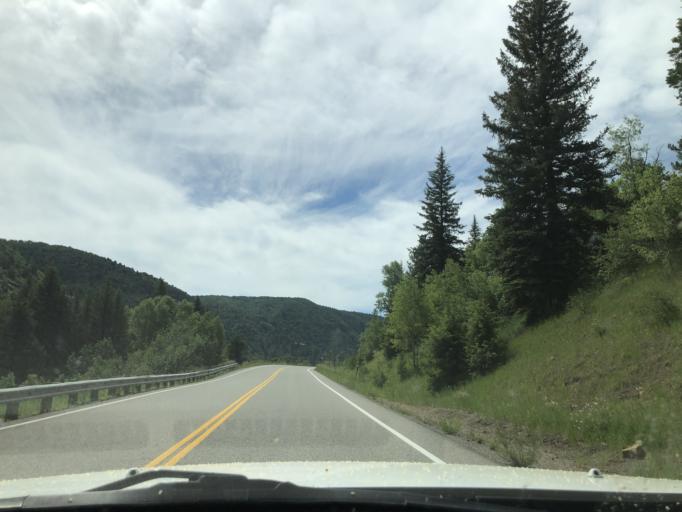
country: US
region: Colorado
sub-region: Delta County
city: Paonia
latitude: 38.9810
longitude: -107.3460
